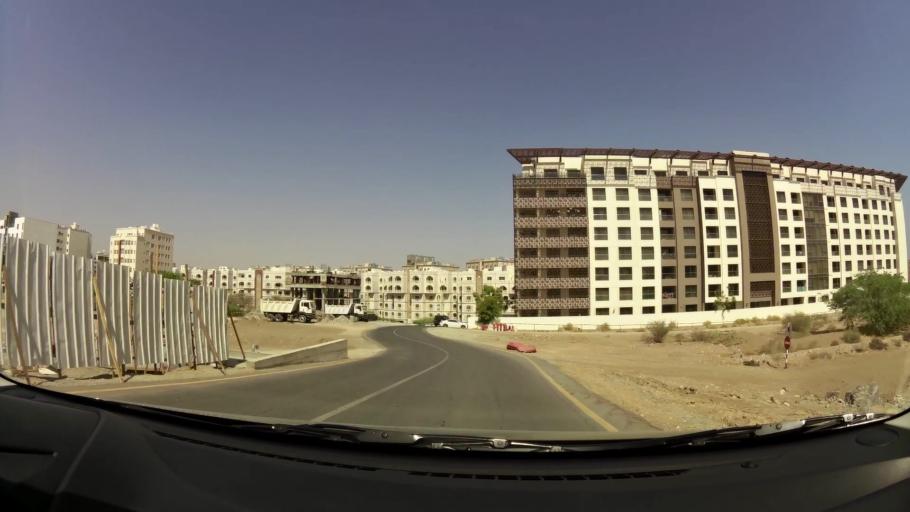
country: OM
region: Muhafazat Masqat
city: Bawshar
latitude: 23.5829
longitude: 58.4115
